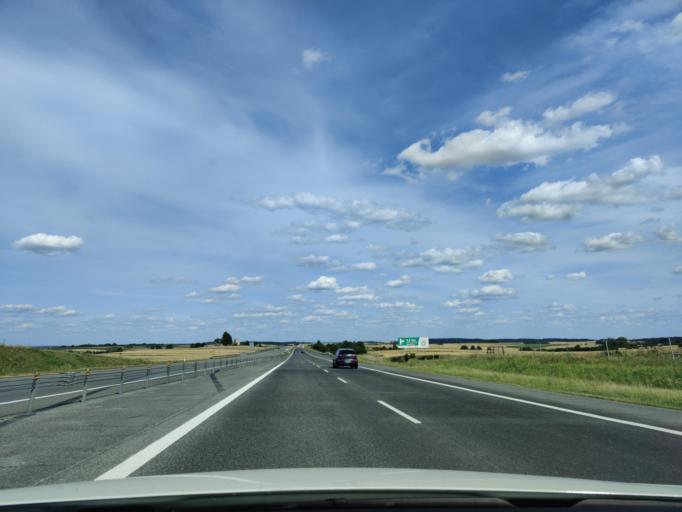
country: PL
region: Opole Voivodeship
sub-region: Powiat strzelecki
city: Lesnica
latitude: 50.4677
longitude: 18.1803
